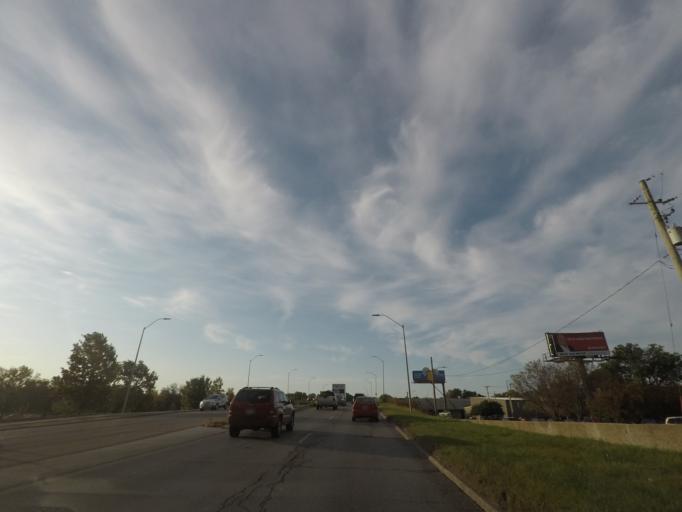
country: US
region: Iowa
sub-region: Polk County
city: Des Moines
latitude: 41.5680
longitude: -93.6450
